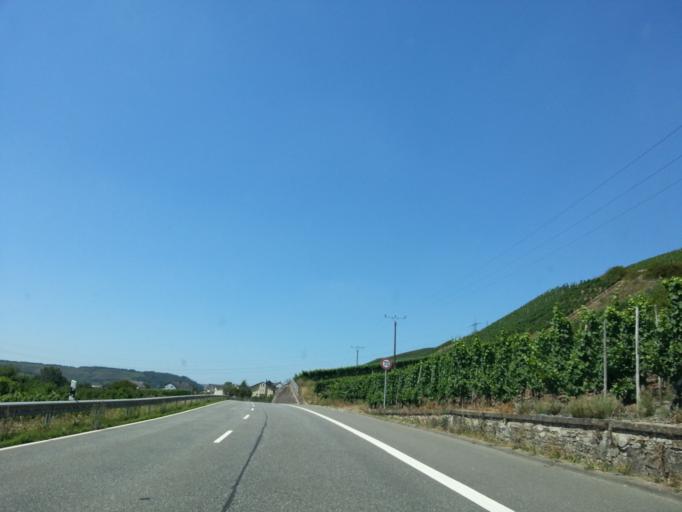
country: DE
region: Rheinland-Pfalz
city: Longuich
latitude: 49.8023
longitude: 6.7952
